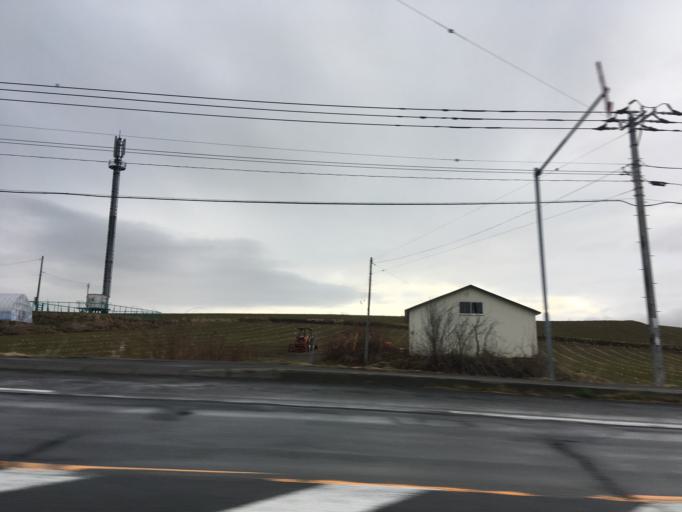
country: JP
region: Hokkaido
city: Nayoro
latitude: 44.0640
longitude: 142.3997
